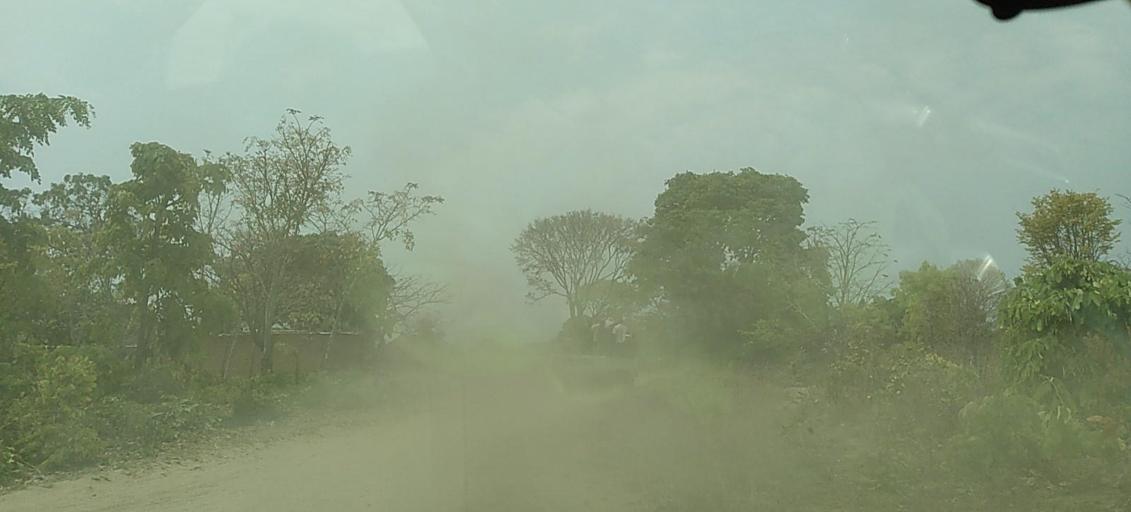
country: ZM
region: North-Western
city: Kabompo
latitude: -13.4819
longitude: 24.4596
